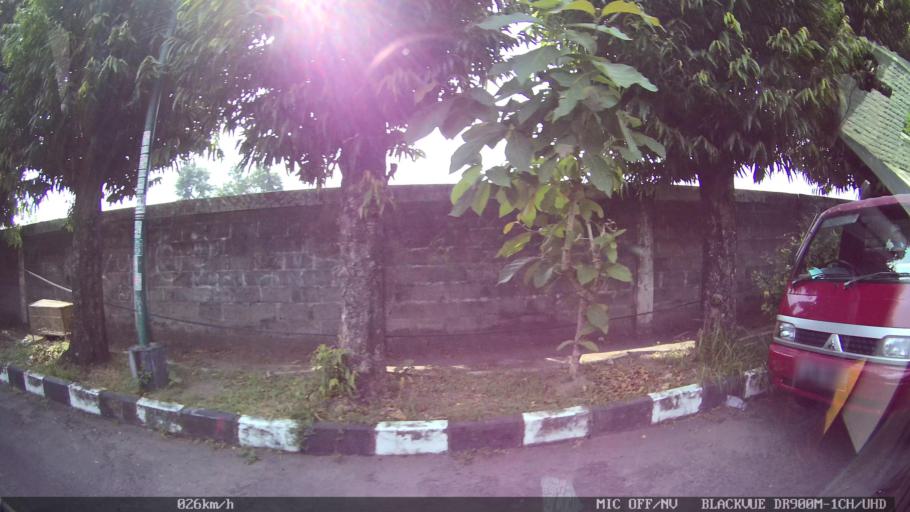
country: ID
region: Daerah Istimewa Yogyakarta
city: Yogyakarta
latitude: -7.7966
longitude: 110.3872
